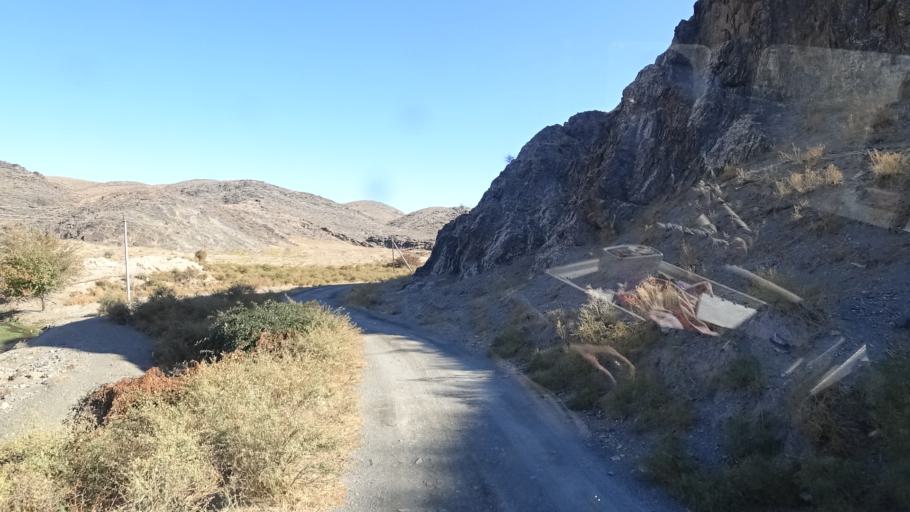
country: UZ
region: Navoiy
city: Nurota
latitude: 40.2985
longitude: 65.6071
